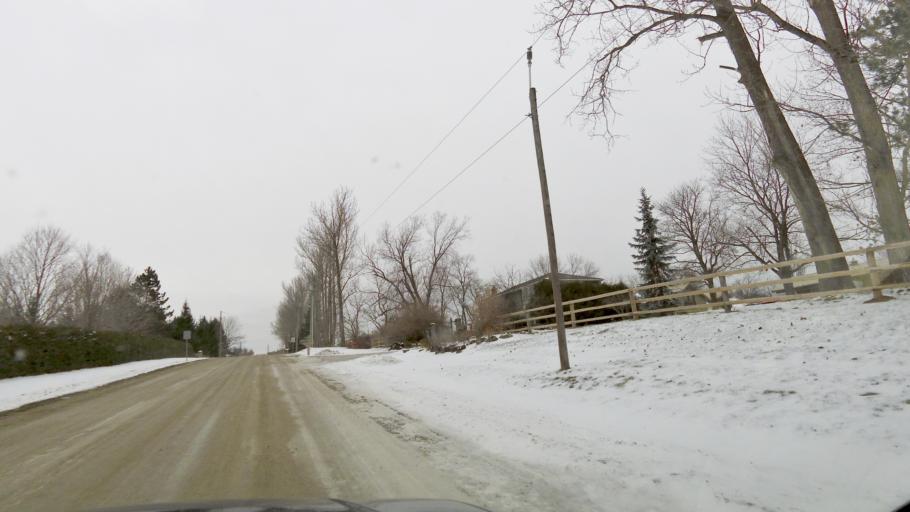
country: CA
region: Ontario
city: Vaughan
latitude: 43.9242
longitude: -79.6061
